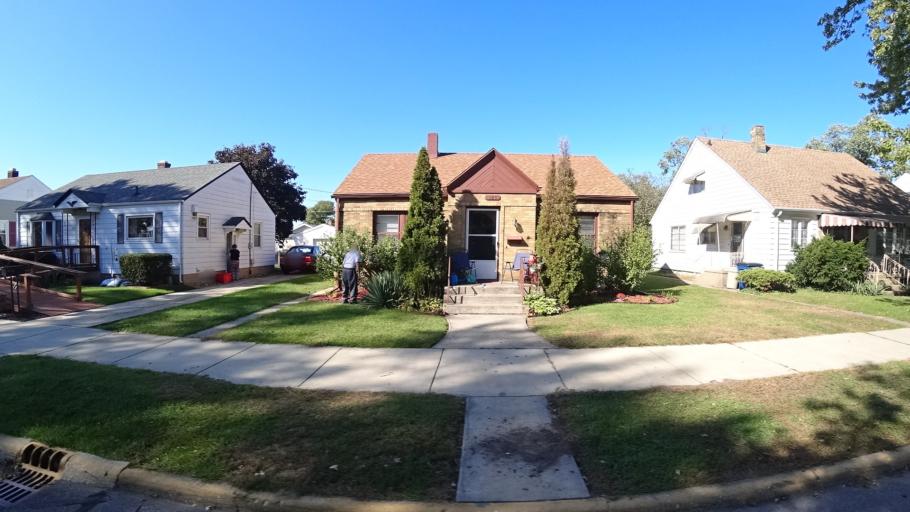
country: US
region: Indiana
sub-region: LaPorte County
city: Michigan City
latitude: 41.7049
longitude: -86.8878
